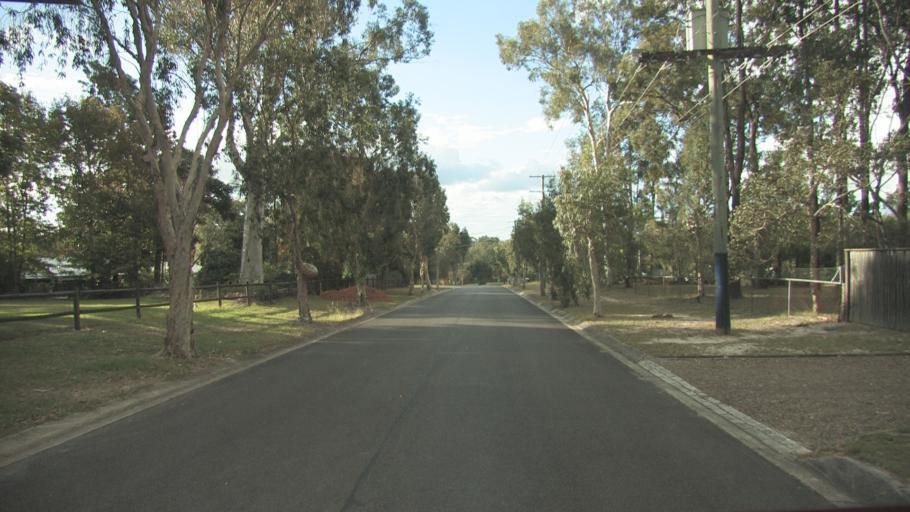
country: AU
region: Queensland
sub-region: Logan
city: Park Ridge South
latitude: -27.7057
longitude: 153.0204
